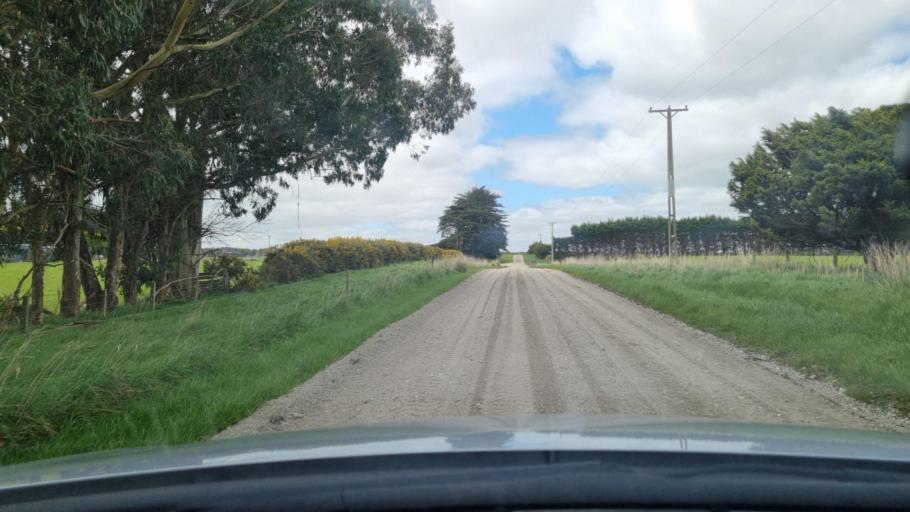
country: NZ
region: Southland
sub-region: Invercargill City
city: Invercargill
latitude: -46.4342
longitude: 168.4076
